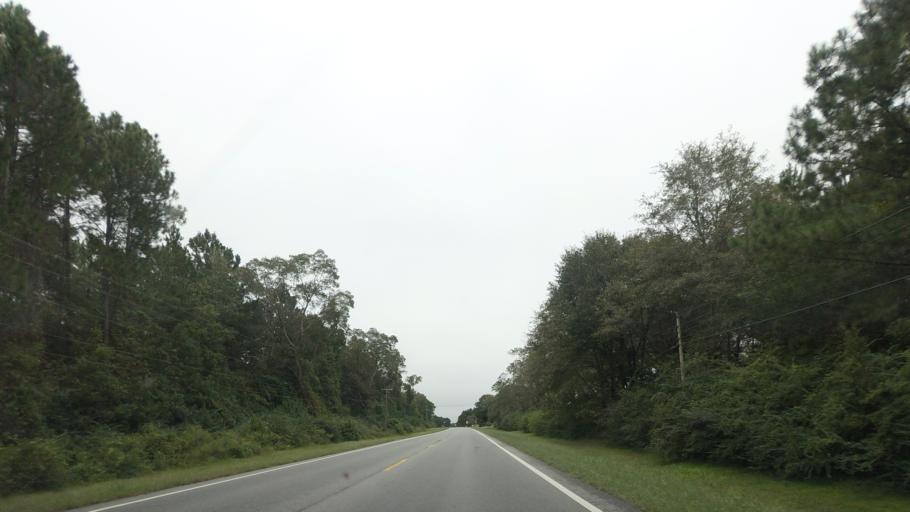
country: US
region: Georgia
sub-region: Berrien County
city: Nashville
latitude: 31.2285
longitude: -83.2471
